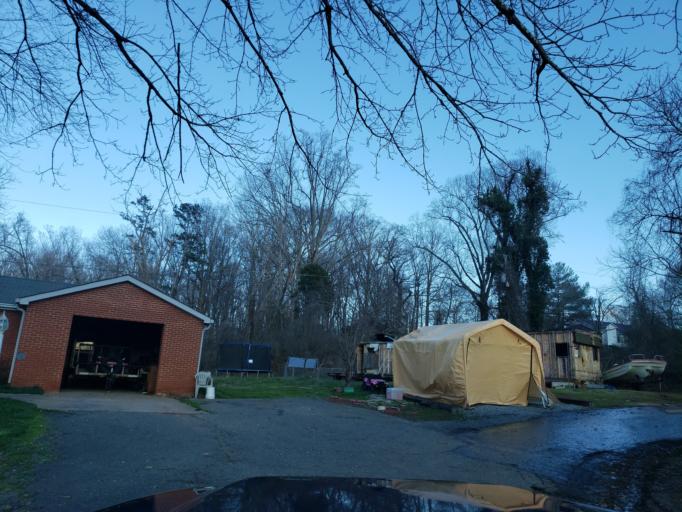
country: US
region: North Carolina
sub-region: Cleveland County
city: Shelby
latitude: 35.4186
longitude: -81.5575
